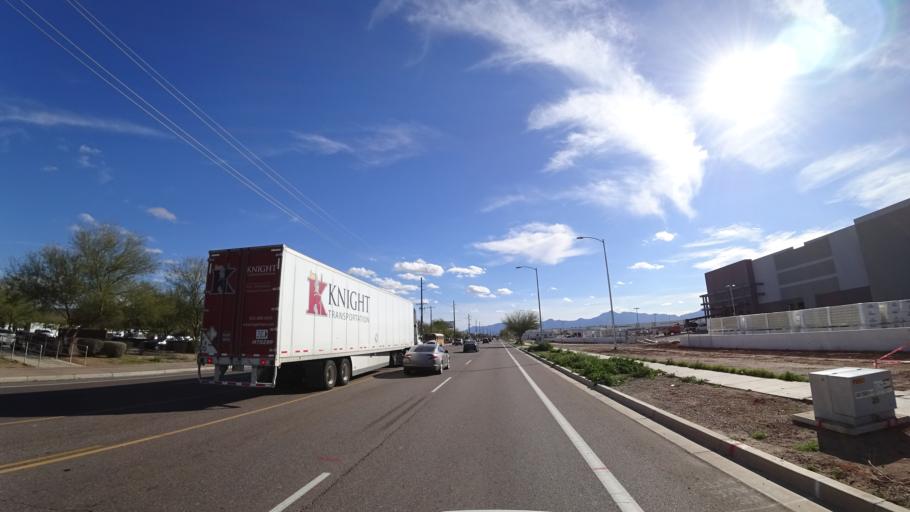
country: US
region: Arizona
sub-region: Maricopa County
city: Tolleson
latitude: 33.4414
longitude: -112.2212
